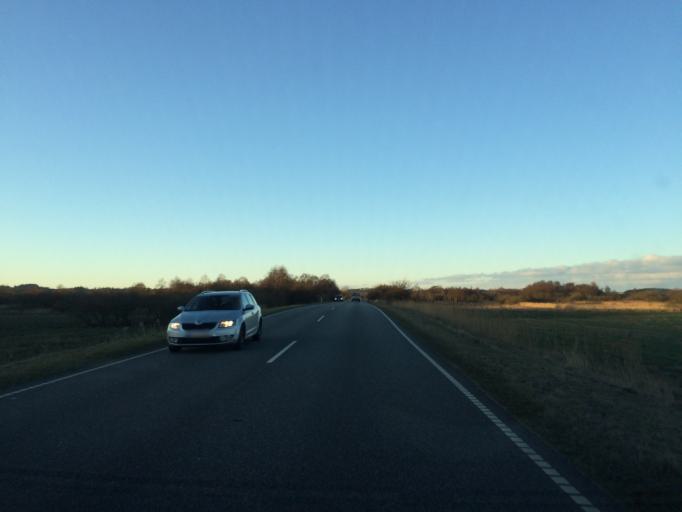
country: DK
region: Central Jutland
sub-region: Randers Kommune
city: Langa
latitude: 56.4878
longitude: 9.8636
